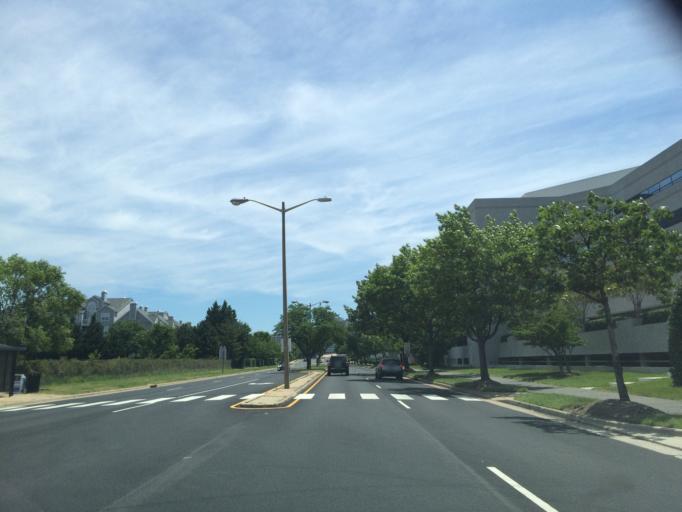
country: US
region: Virginia
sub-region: Fairfax County
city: Huntington
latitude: 38.8026
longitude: -77.0823
